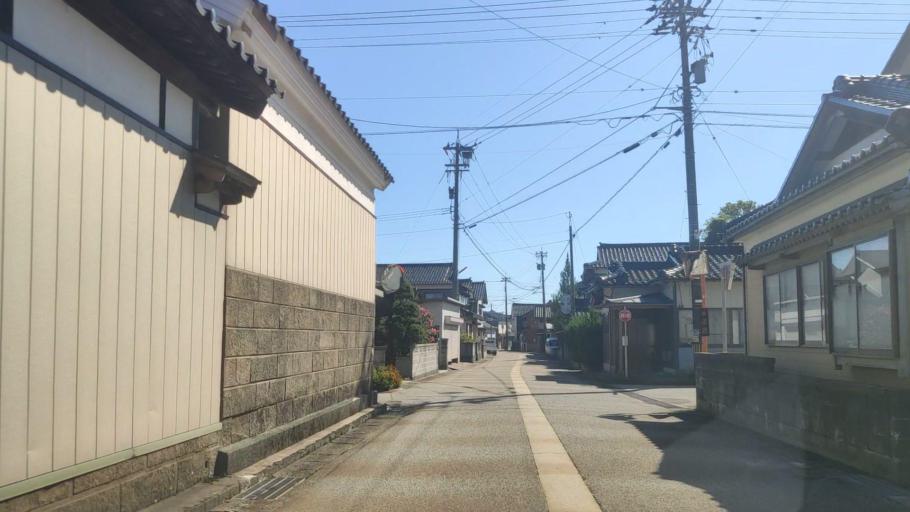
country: JP
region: Ishikawa
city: Nanao
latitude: 37.4460
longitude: 137.2894
